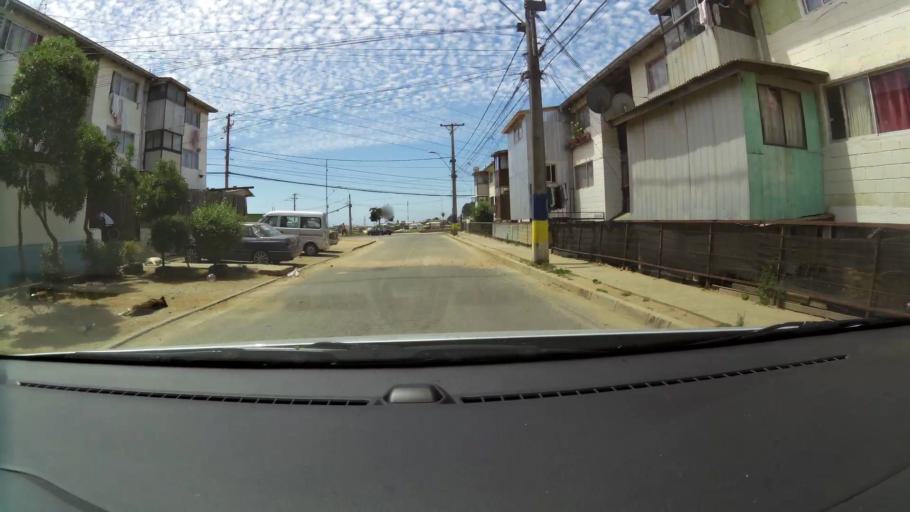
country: CL
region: Valparaiso
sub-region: Provincia de Valparaiso
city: Vina del Mar
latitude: -33.0580
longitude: -71.5606
